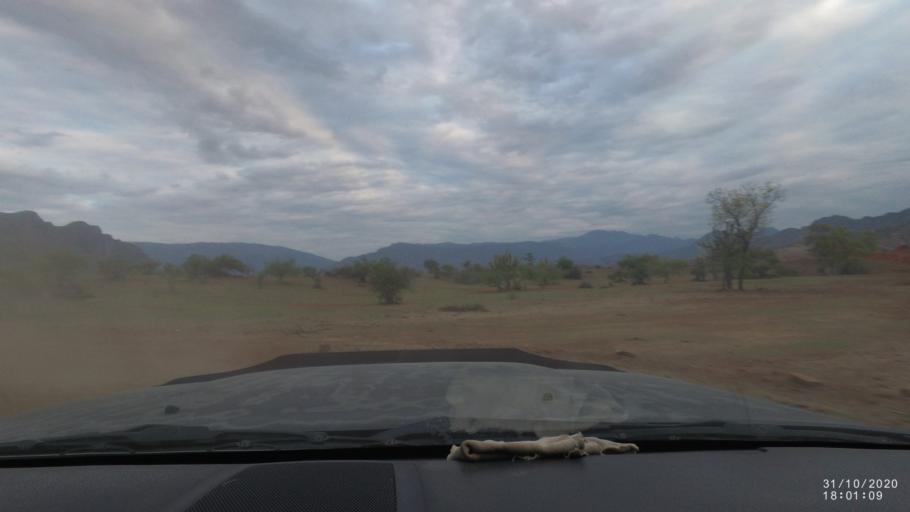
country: BO
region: Chuquisaca
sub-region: Provincia Zudanez
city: Mojocoya
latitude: -18.6651
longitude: -64.5321
